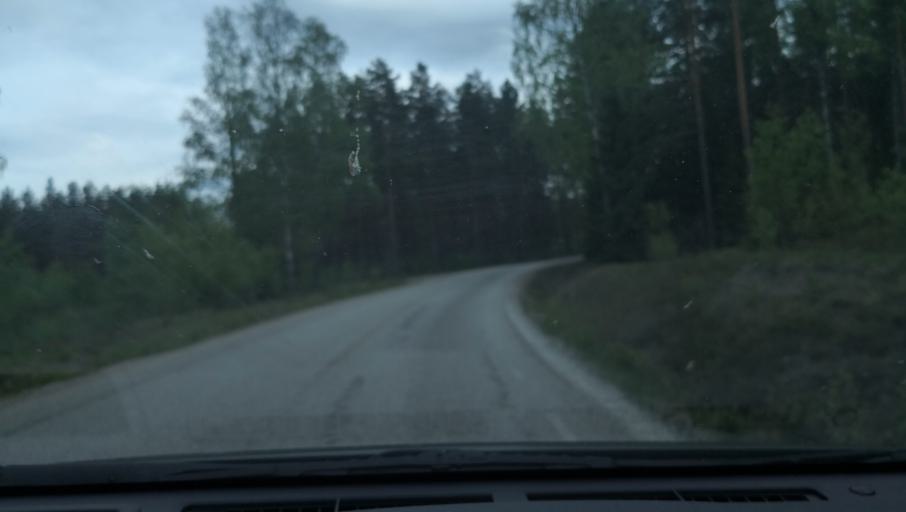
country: SE
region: Vaestmanland
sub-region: Skinnskattebergs Kommun
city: Skinnskatteberg
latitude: 59.8119
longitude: 15.5583
